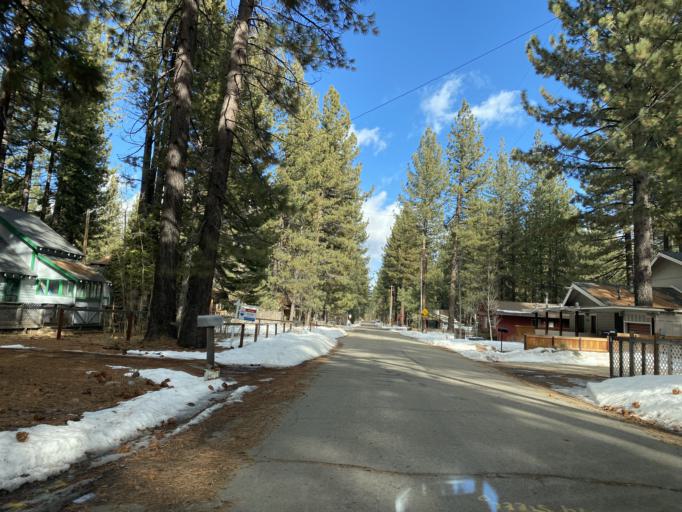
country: US
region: California
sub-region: El Dorado County
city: South Lake Tahoe
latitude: 38.9188
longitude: -119.9807
